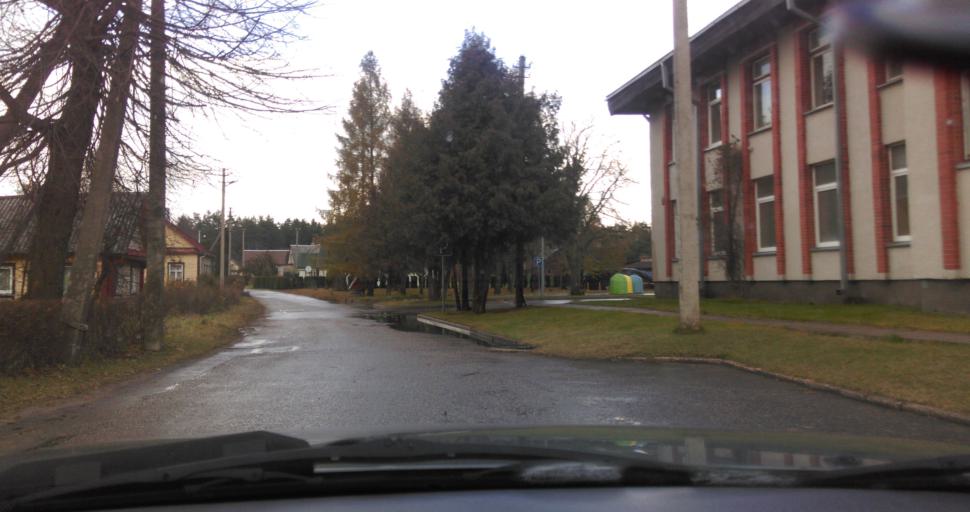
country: LT
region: Utenos apskritis
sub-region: Utena
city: Utena
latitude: 55.5875
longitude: 25.4977
